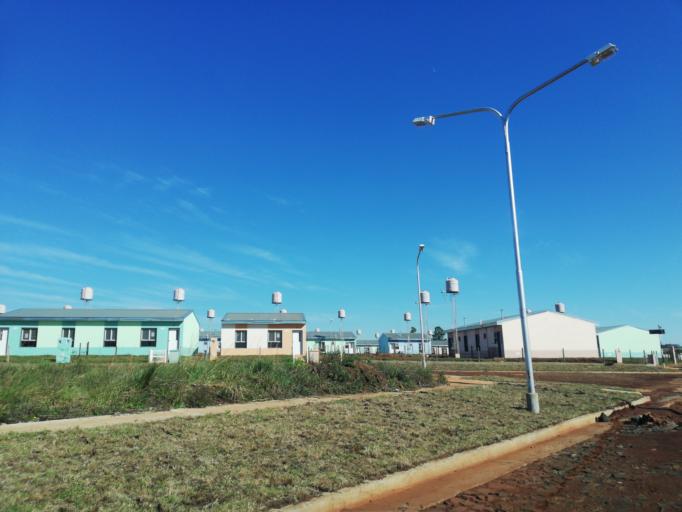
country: AR
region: Misiones
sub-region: Departamento de Capital
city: Posadas
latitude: -27.3997
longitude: -55.9936
